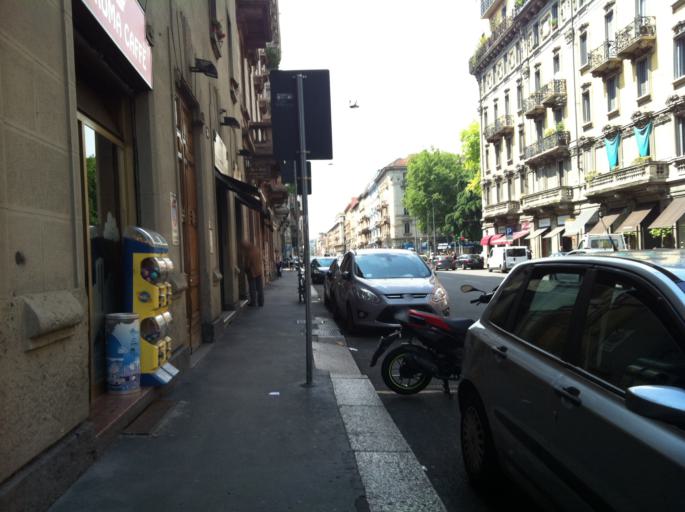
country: IT
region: Lombardy
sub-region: Citta metropolitana di Milano
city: Milano
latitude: 45.4784
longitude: 9.2142
